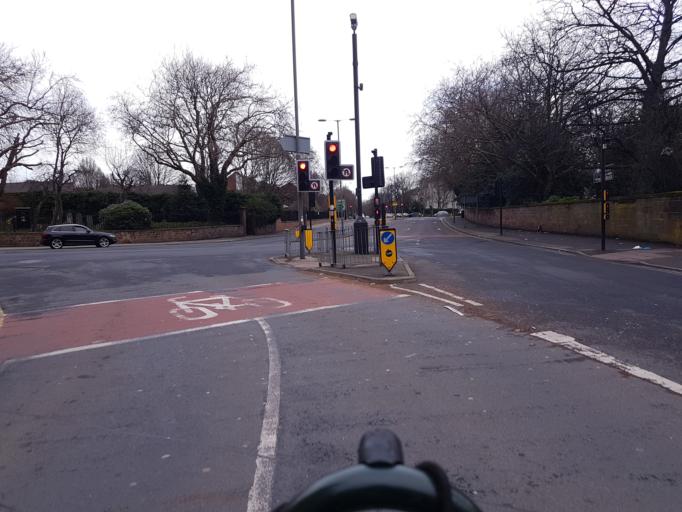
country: GB
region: England
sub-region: Liverpool
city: Liverpool
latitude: 53.3807
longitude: -2.9577
